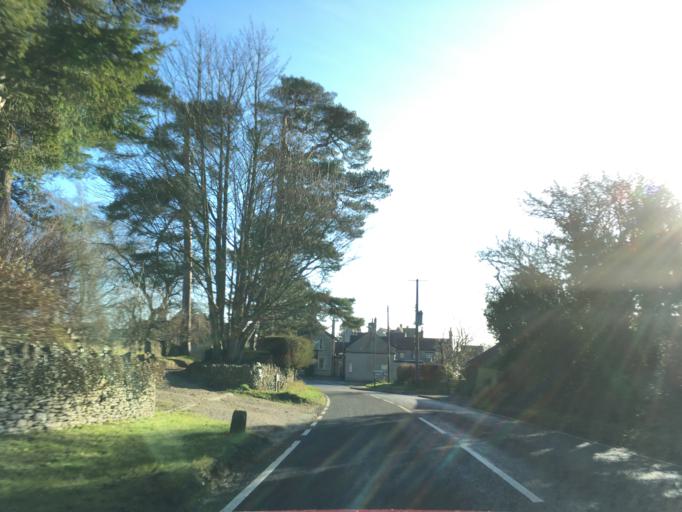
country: GB
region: England
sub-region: Wiltshire
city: Nettleton
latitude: 51.5259
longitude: -2.2789
